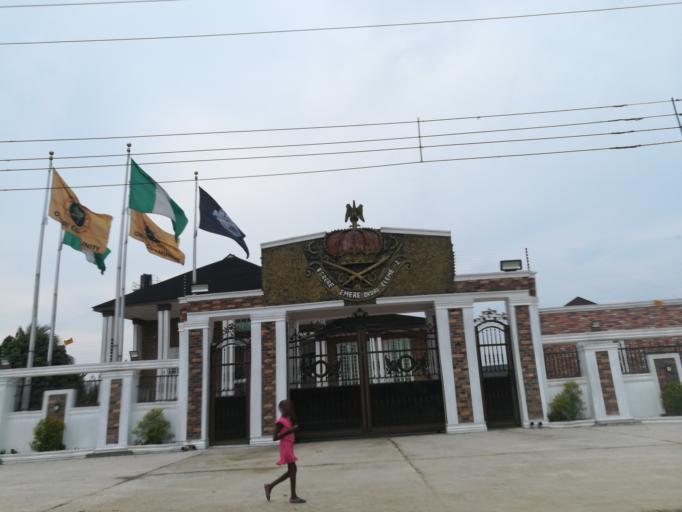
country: NG
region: Rivers
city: Okrika
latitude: 4.7839
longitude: 7.1302
